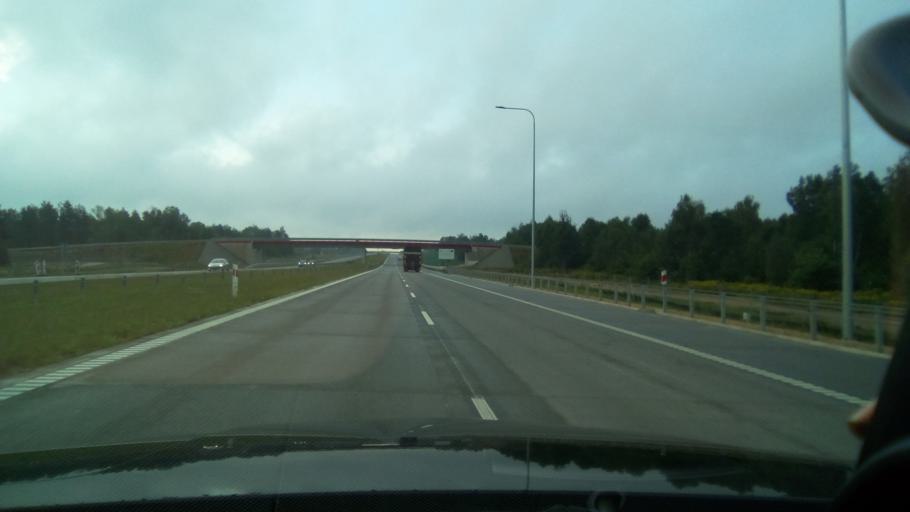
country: PL
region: Silesian Voivodeship
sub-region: Powiat czestochowski
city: Konopiska
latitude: 50.7734
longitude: 19.0100
